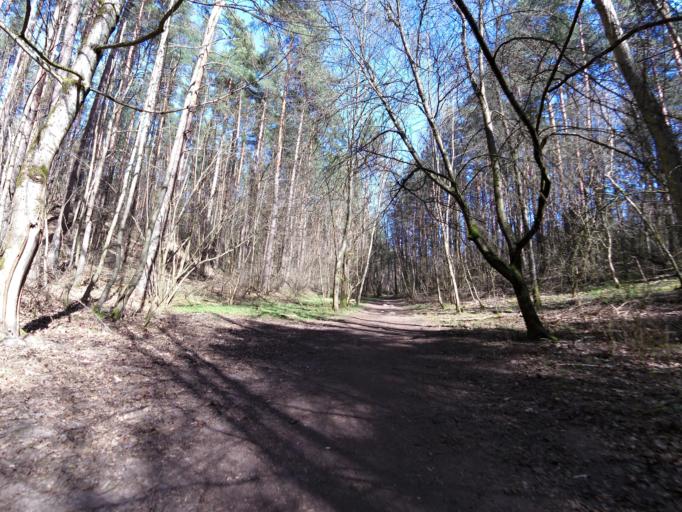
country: LT
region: Vilnius County
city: Pilaite
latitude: 54.6937
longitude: 25.1996
